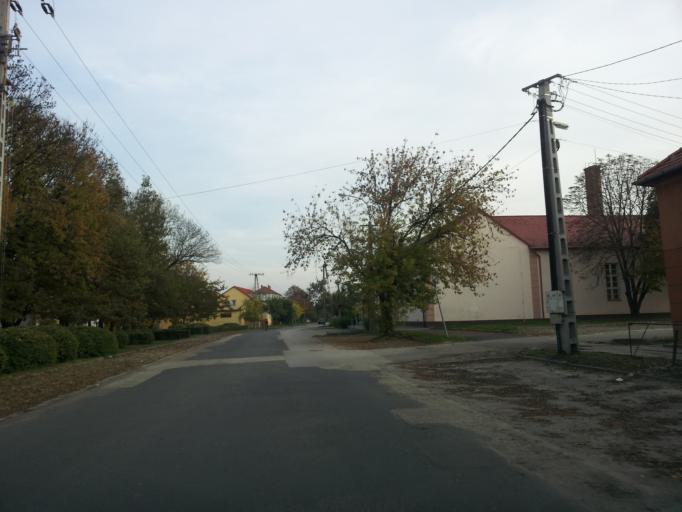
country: HU
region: Pest
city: Nagykata
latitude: 47.4164
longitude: 19.7434
